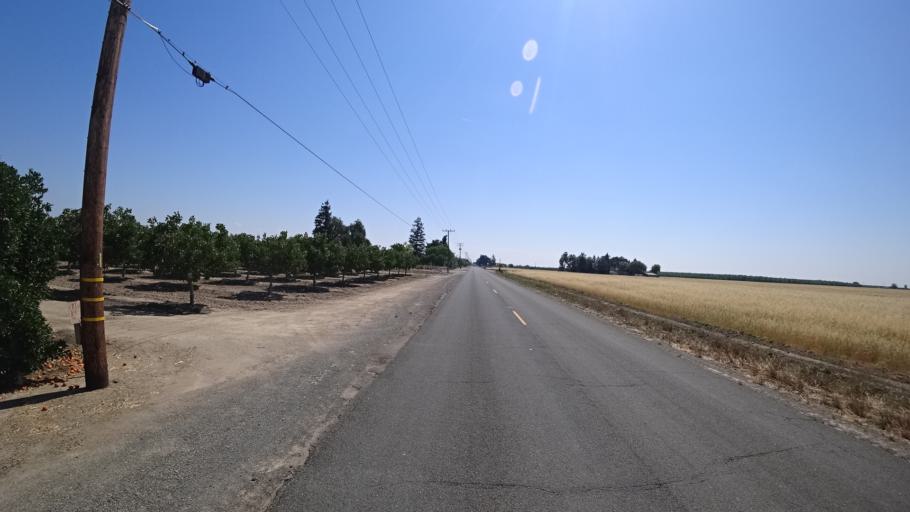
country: US
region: California
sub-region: Kings County
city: Lucerne
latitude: 36.3718
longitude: -119.6164
